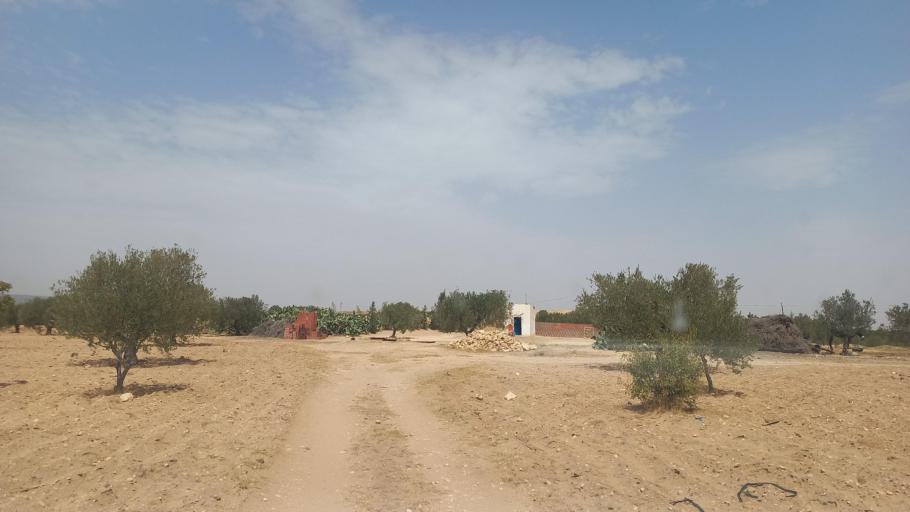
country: TN
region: Al Qasrayn
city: Kasserine
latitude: 35.2664
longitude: 8.9843
